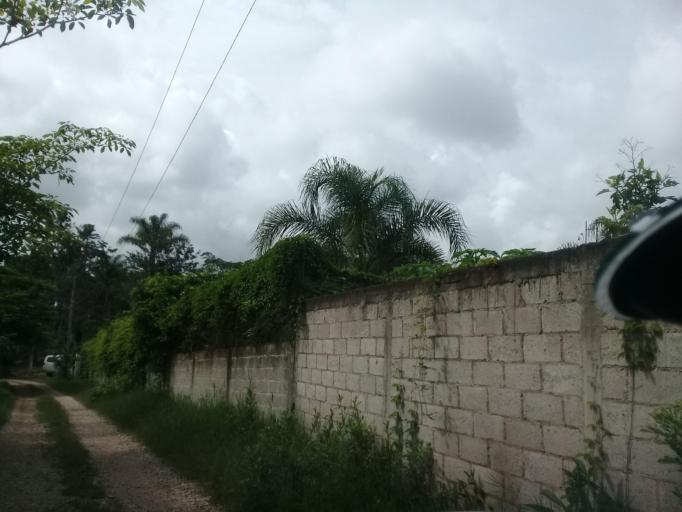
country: MX
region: Veracruz
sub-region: Emiliano Zapata
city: Jacarandas
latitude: 19.4827
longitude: -96.8540
